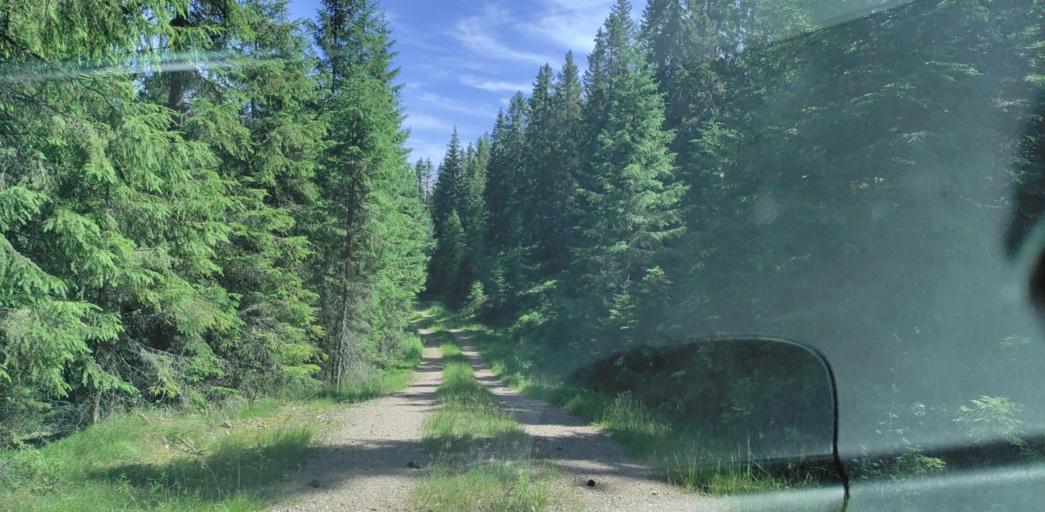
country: SE
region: Vaermland
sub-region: Hagfors Kommun
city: Ekshaerad
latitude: 60.0881
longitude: 13.3772
